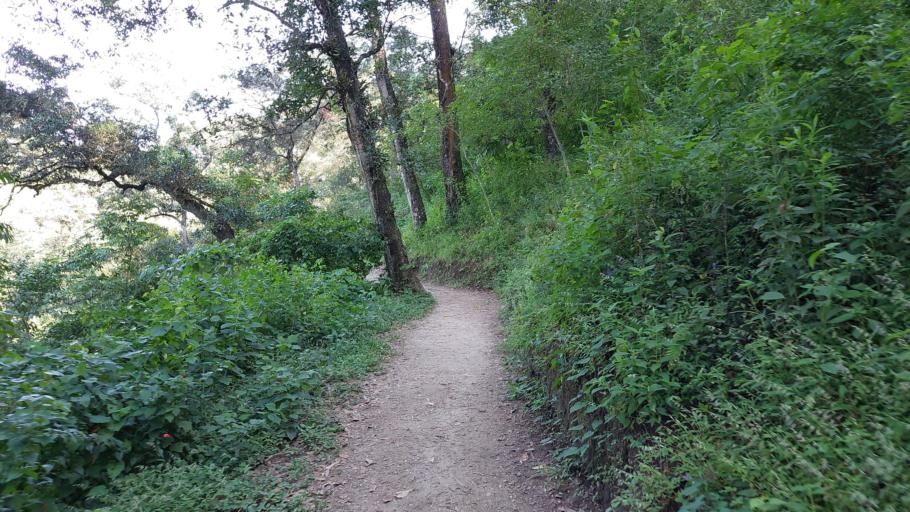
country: GT
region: Guatemala
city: Guatemala City
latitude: 14.6400
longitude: -90.4942
